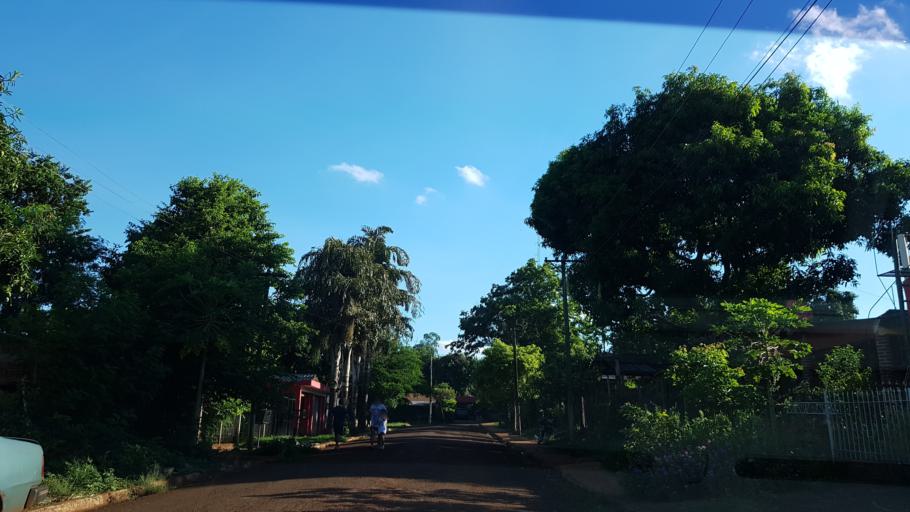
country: AR
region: Misiones
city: Puerto Libertad
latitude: -25.9180
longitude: -54.5888
